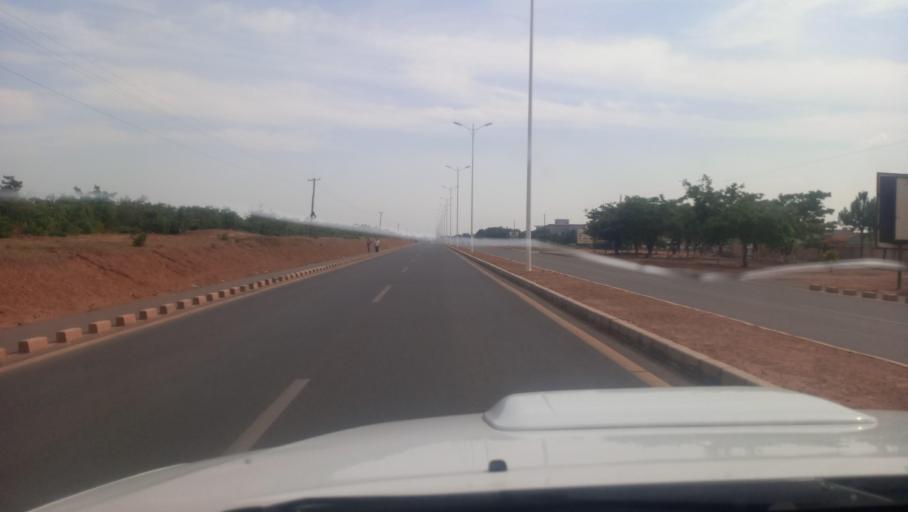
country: ZM
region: Northern
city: Mpika
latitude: -11.8476
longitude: 31.4426
